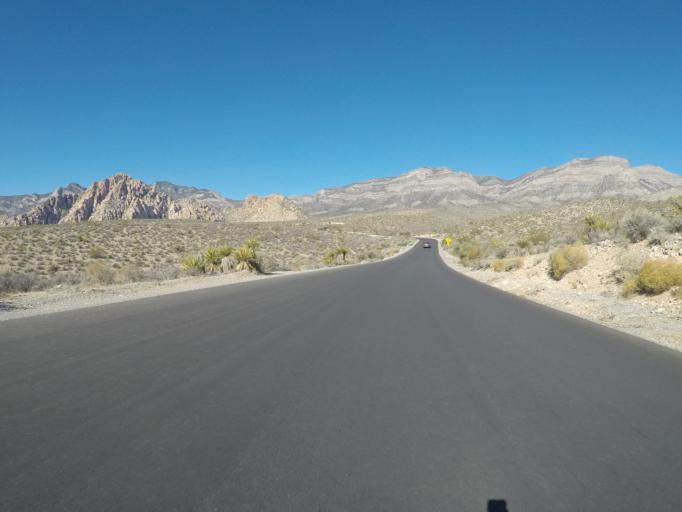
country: US
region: Nevada
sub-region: Clark County
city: Summerlin South
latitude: 36.1604
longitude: -115.4580
